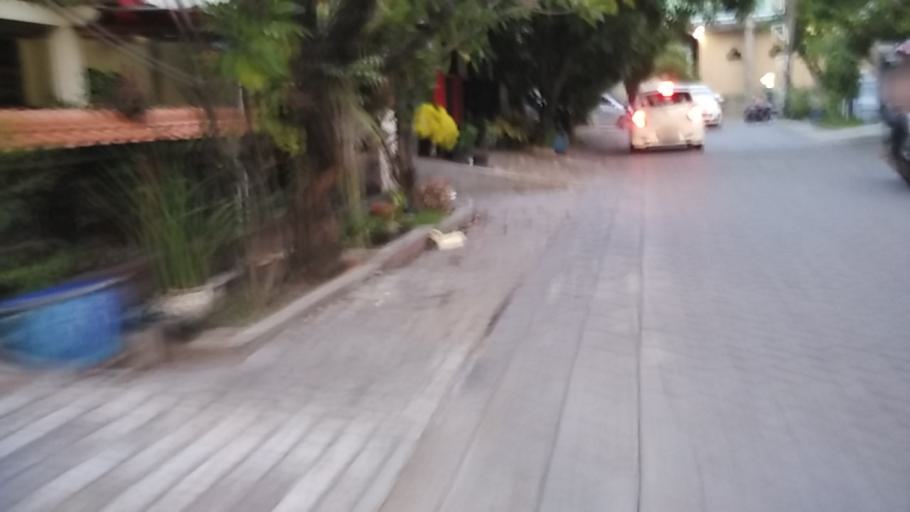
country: ID
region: Central Java
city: Semarang
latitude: -6.9821
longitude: 110.4550
